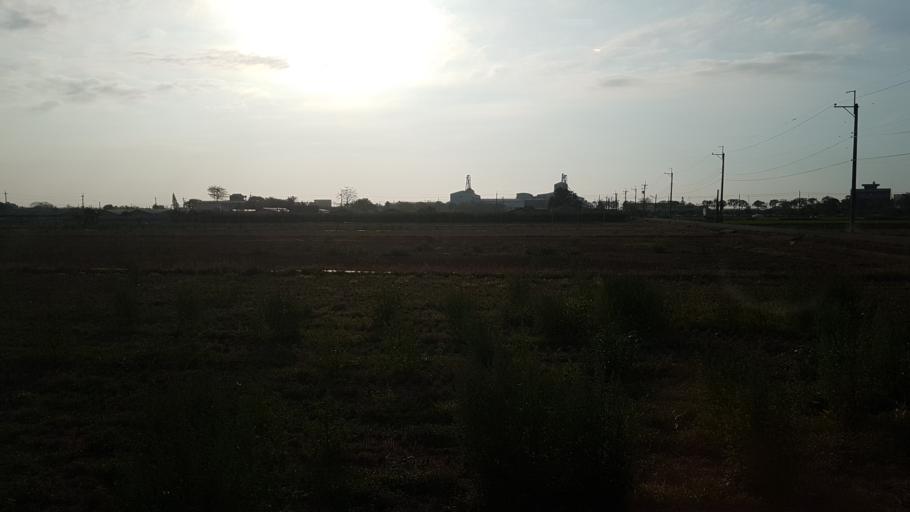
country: TW
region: Taiwan
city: Xinying
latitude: 23.3462
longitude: 120.3590
